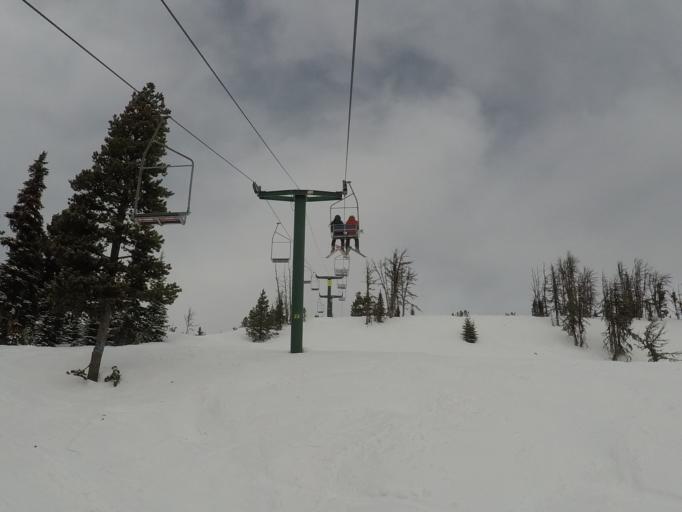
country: US
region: Montana
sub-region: Meagher County
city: White Sulphur Springs
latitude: 46.8371
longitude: -110.7152
